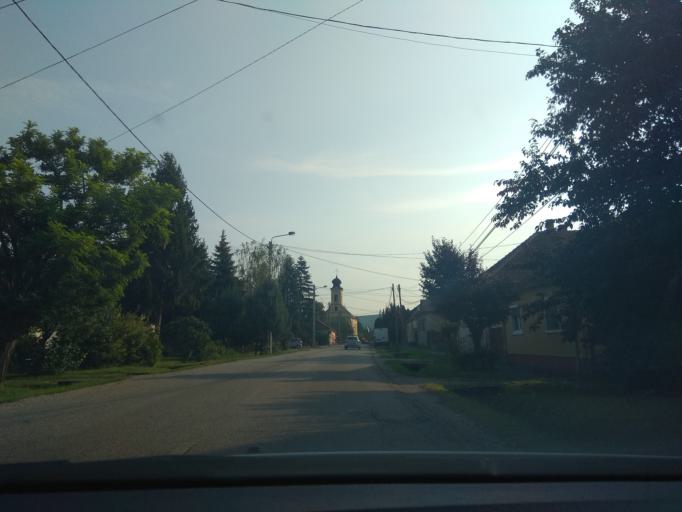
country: HU
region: Heves
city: Felsotarkany
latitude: 47.9703
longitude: 20.4115
